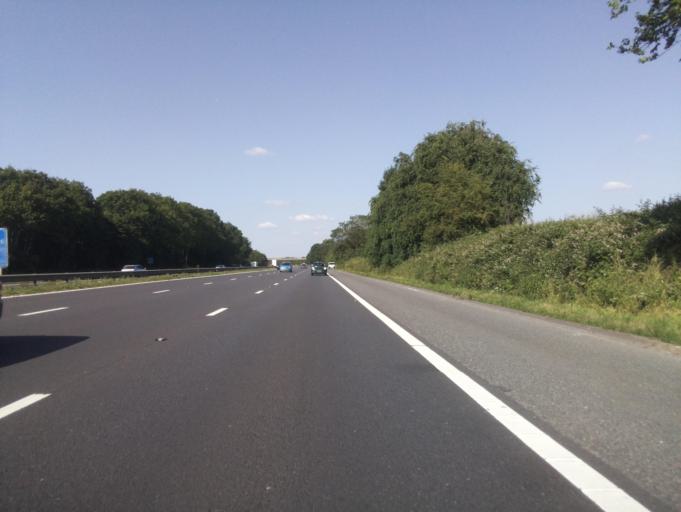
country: GB
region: England
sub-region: Gloucestershire
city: Uckington
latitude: 51.9345
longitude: -2.1332
